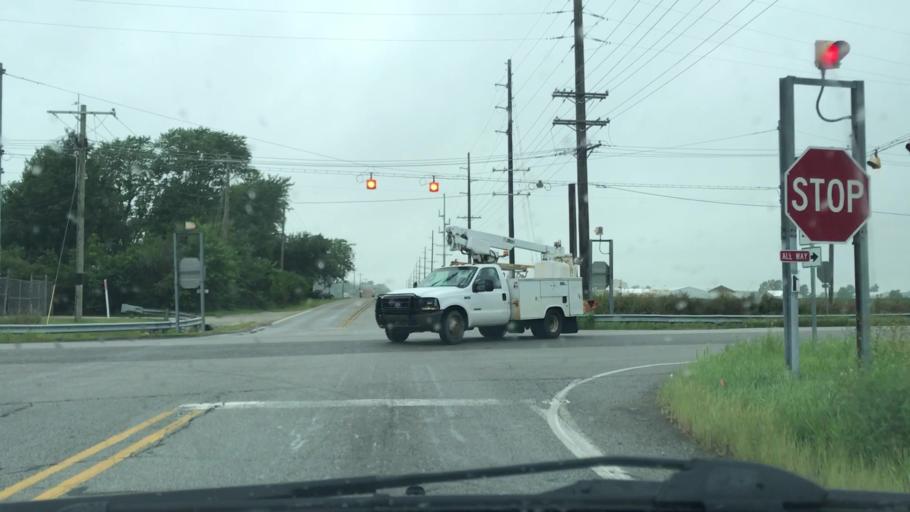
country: US
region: Indiana
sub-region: Hamilton County
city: Sheridan
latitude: 40.1280
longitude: -86.3281
